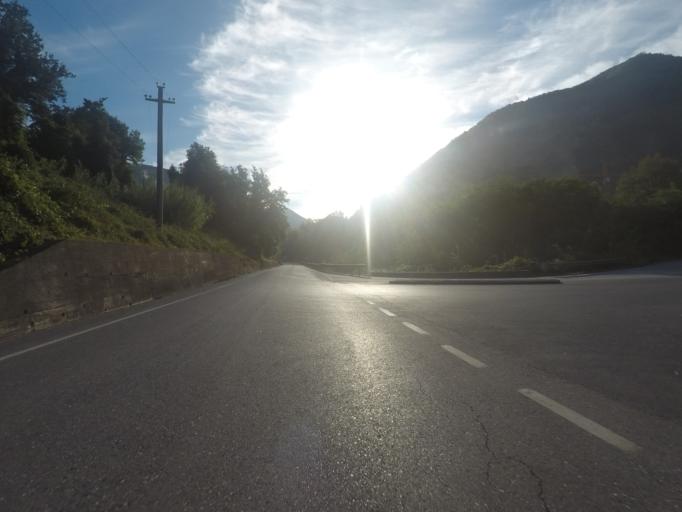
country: IT
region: Tuscany
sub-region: Provincia di Lucca
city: Valdottavo
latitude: 43.9684
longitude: 10.4747
